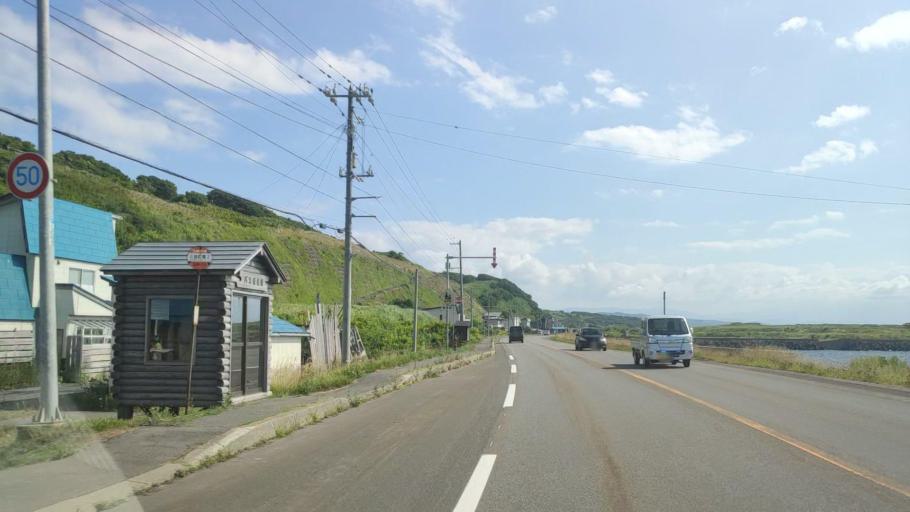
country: JP
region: Hokkaido
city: Rumoi
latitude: 43.9787
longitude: 141.6464
